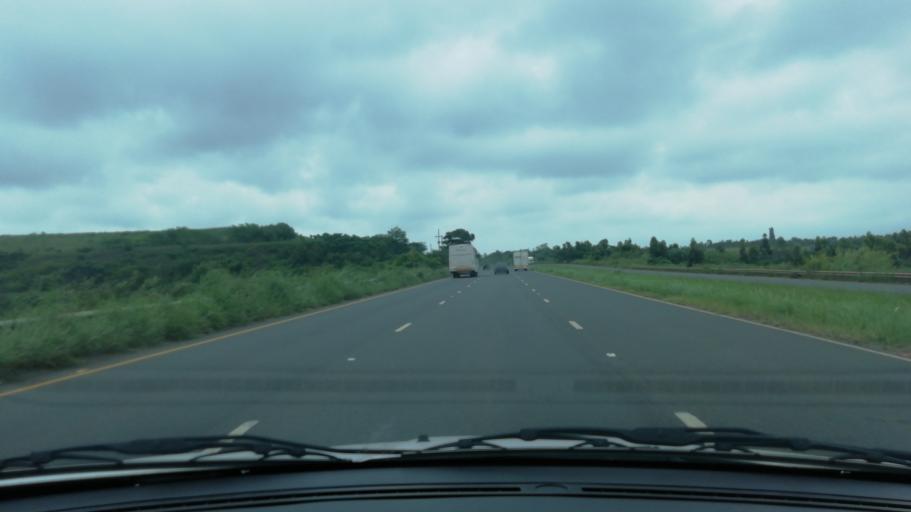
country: ZA
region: KwaZulu-Natal
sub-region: uThungulu District Municipality
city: Empangeni
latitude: -28.7677
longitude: 31.9248
